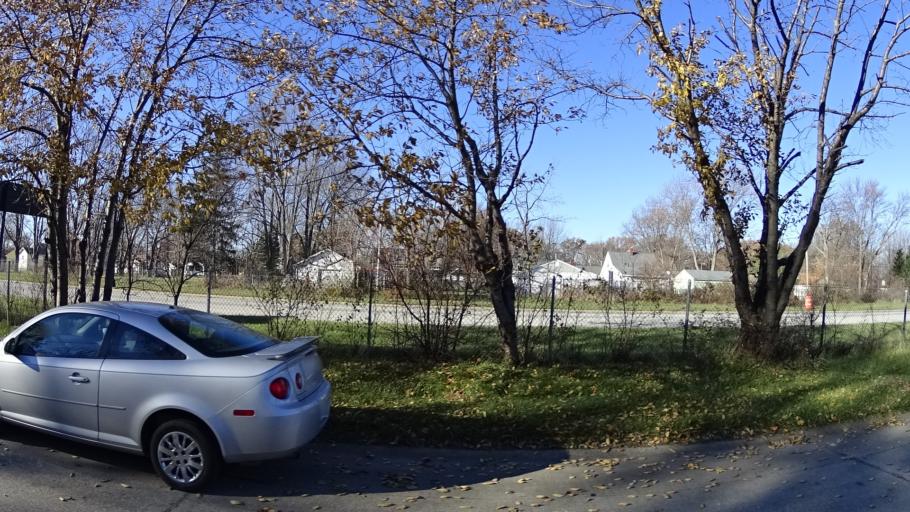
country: US
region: Ohio
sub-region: Lorain County
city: Elyria
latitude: 41.3835
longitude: -82.0751
